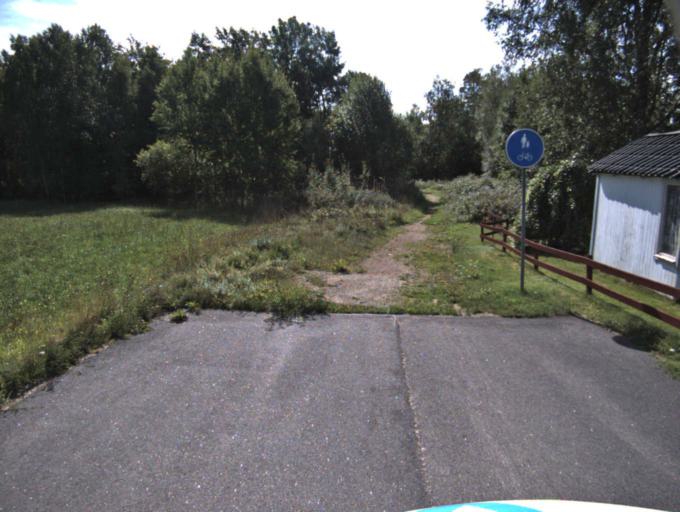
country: SE
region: Vaestra Goetaland
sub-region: Ulricehamns Kommun
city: Ulricehamn
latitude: 57.9022
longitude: 13.4629
